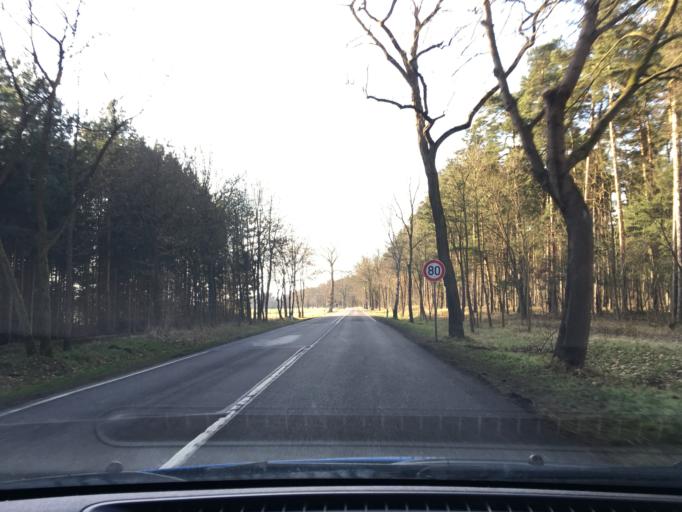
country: DE
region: Saxony-Anhalt
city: Luftkurort Arendsee
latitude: 52.8839
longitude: 11.6118
